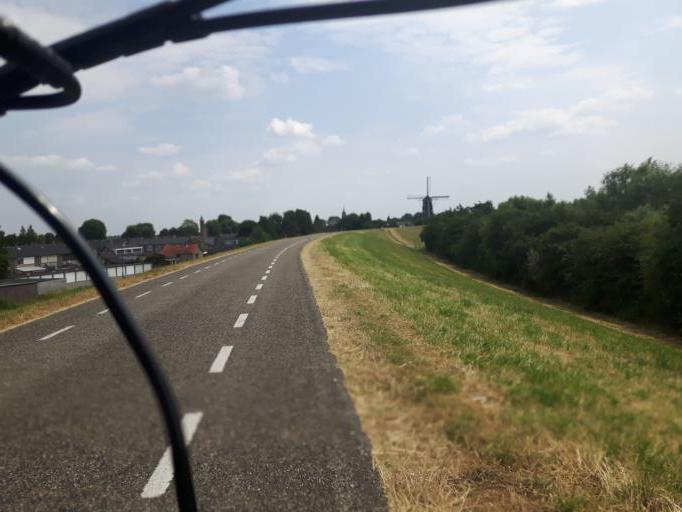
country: NL
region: Gelderland
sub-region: Gemeente Zaltbommel
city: Zaltbommel
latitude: 51.8159
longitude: 5.2069
